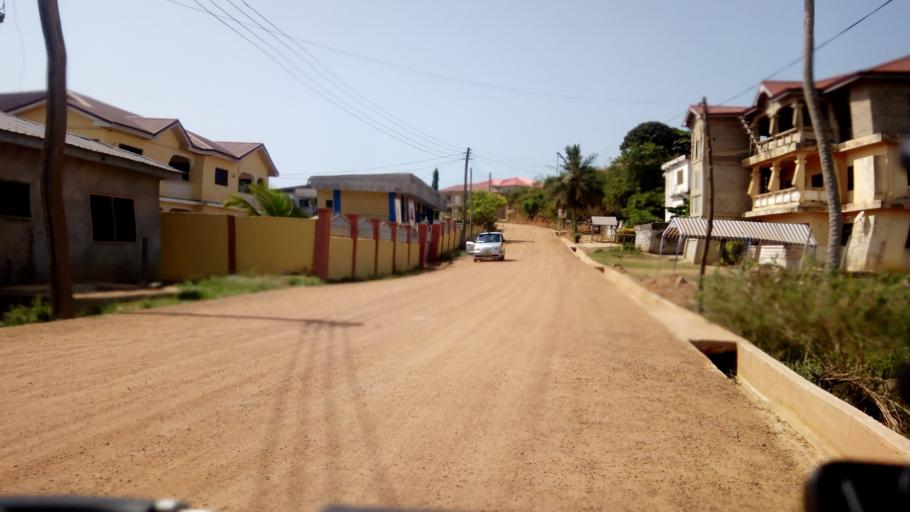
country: GH
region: Central
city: Cape Coast
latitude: 5.1125
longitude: -1.2681
